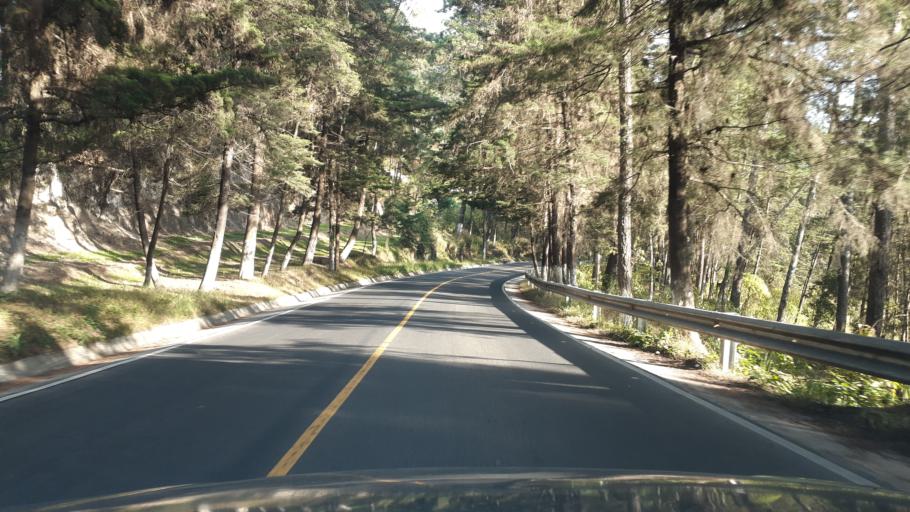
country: GT
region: Chimaltenango
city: El Tejar
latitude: 14.6379
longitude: -90.8134
